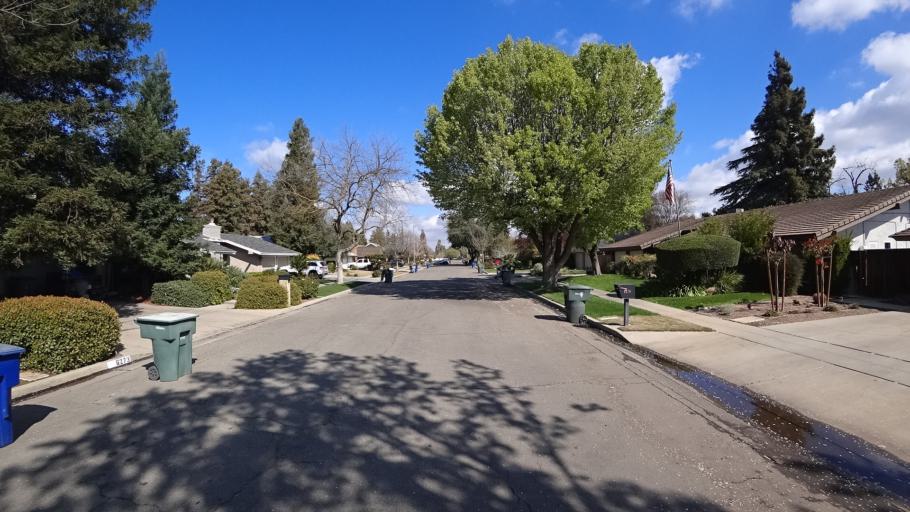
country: US
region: California
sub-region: Fresno County
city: Fresno
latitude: 36.8277
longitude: -119.8518
